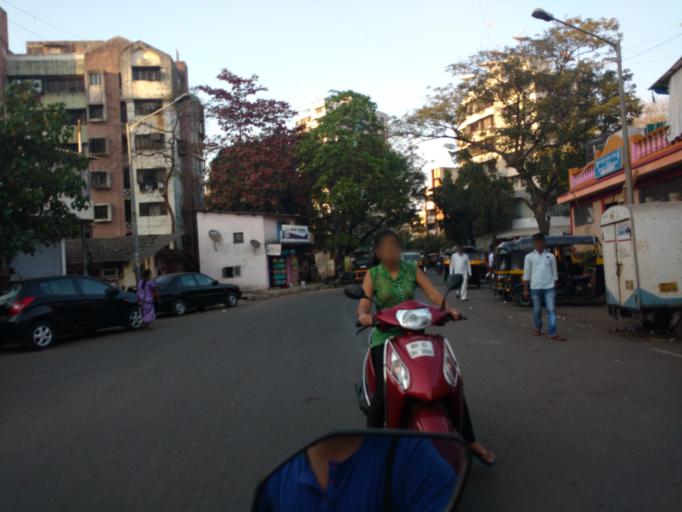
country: IN
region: Maharashtra
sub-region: Mumbai Suburban
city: Borivli
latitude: 19.2049
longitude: 72.8378
